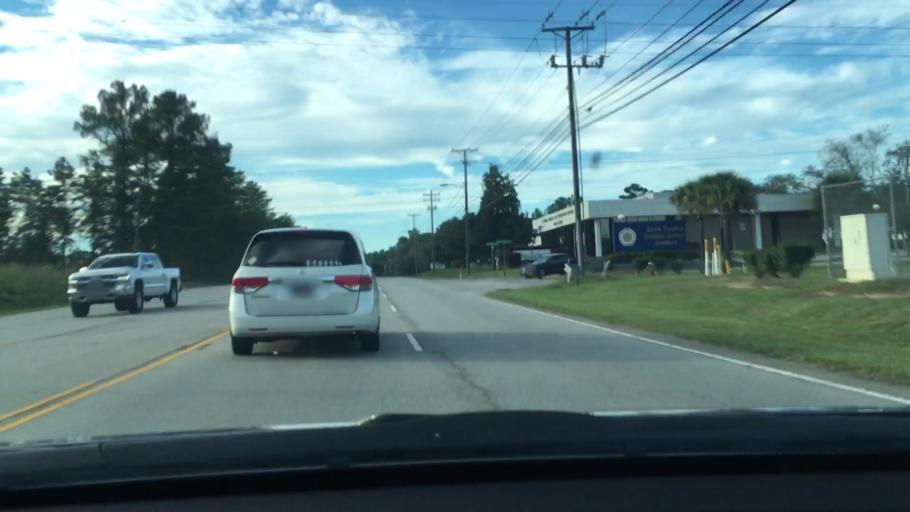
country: US
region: South Carolina
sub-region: Lexington County
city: Saint Andrews
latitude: 34.0757
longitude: -81.1256
